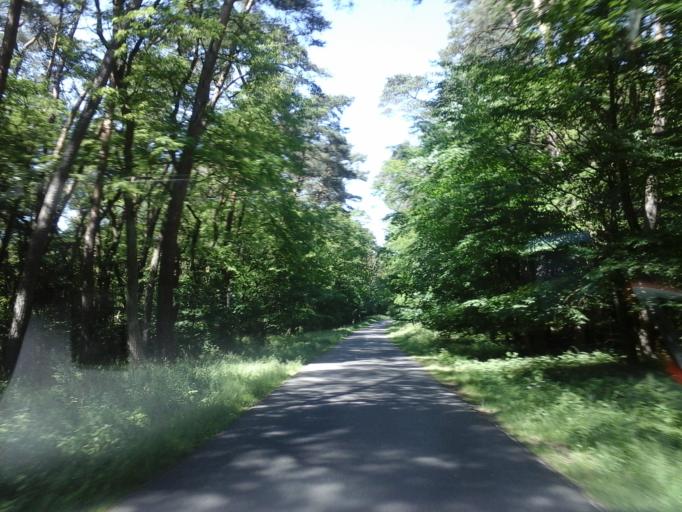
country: PL
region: West Pomeranian Voivodeship
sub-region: Powiat walecki
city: Czlopa
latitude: 53.0616
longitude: 15.9418
